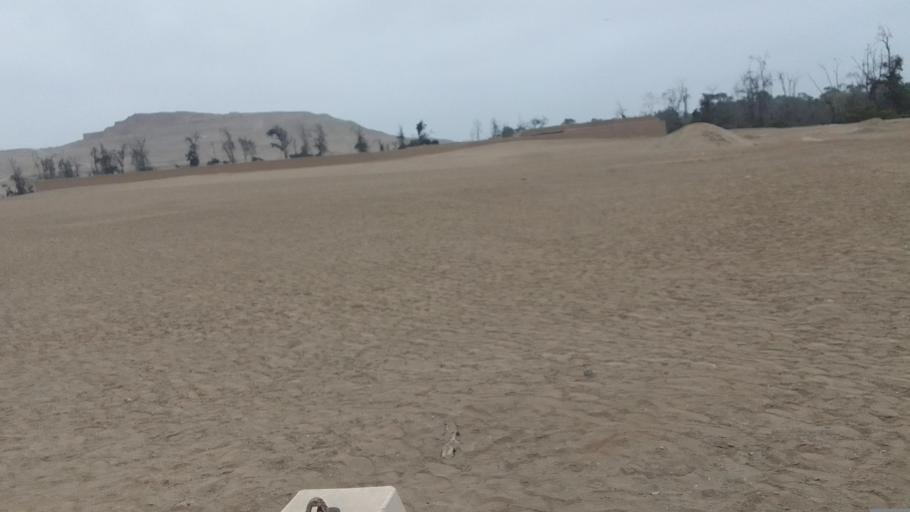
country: PE
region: Lima
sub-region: Lima
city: Punta Hermosa
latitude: -12.2558
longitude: -76.9059
